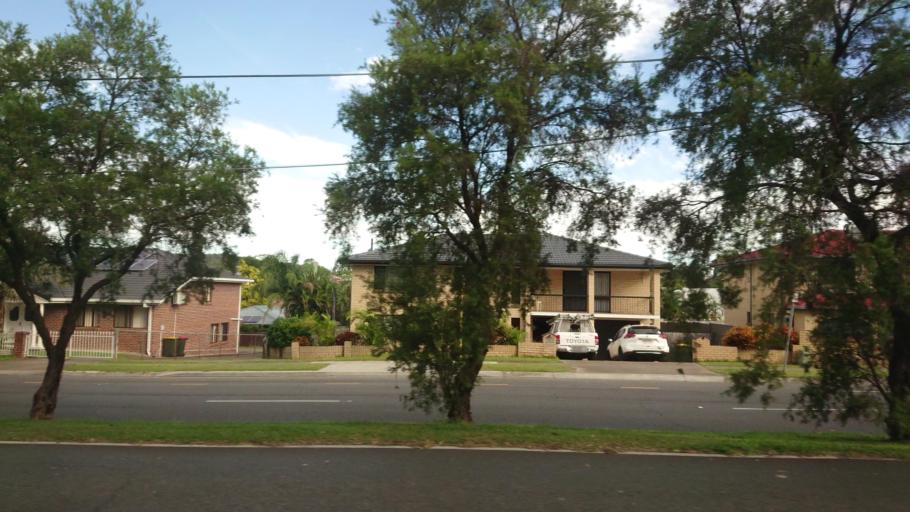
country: AU
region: Queensland
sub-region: Brisbane
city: Belmont
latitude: -27.4928
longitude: 153.1121
